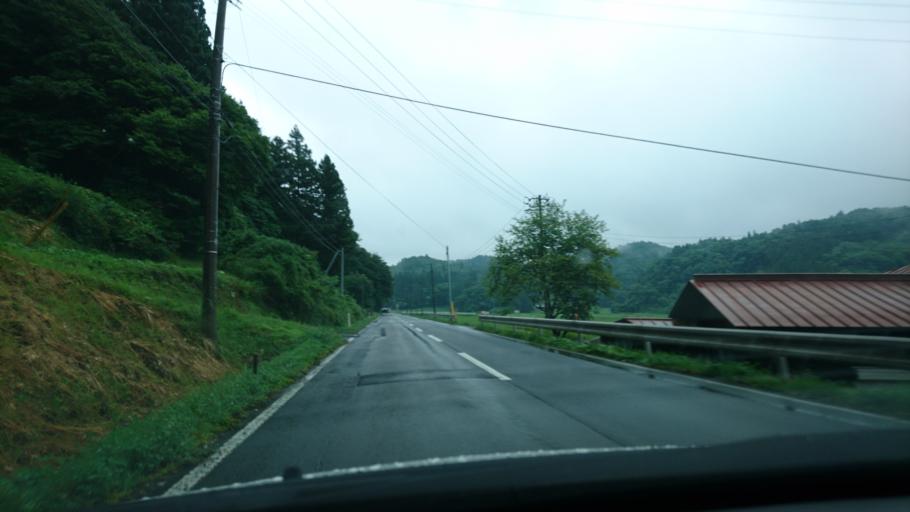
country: JP
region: Iwate
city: Ichinoseki
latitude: 38.9004
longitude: 141.0373
